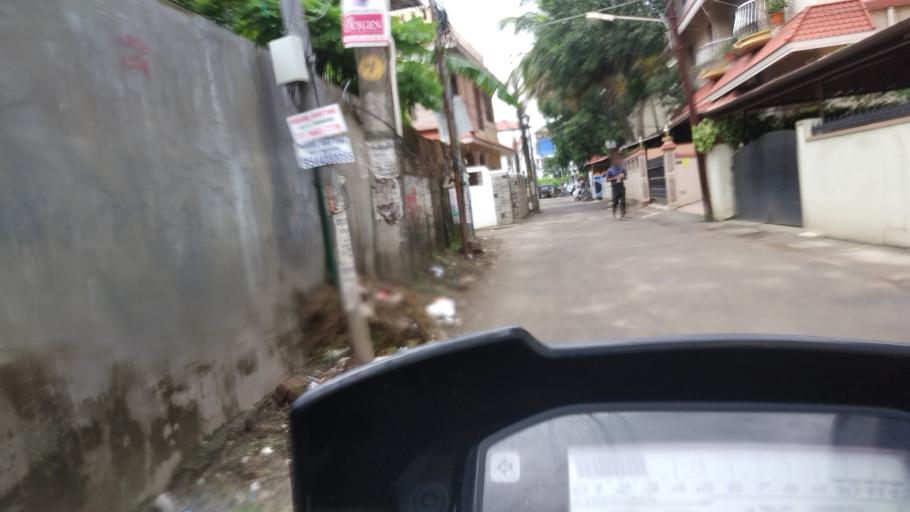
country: IN
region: Kerala
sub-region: Ernakulam
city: Cochin
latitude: 9.9695
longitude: 76.3109
